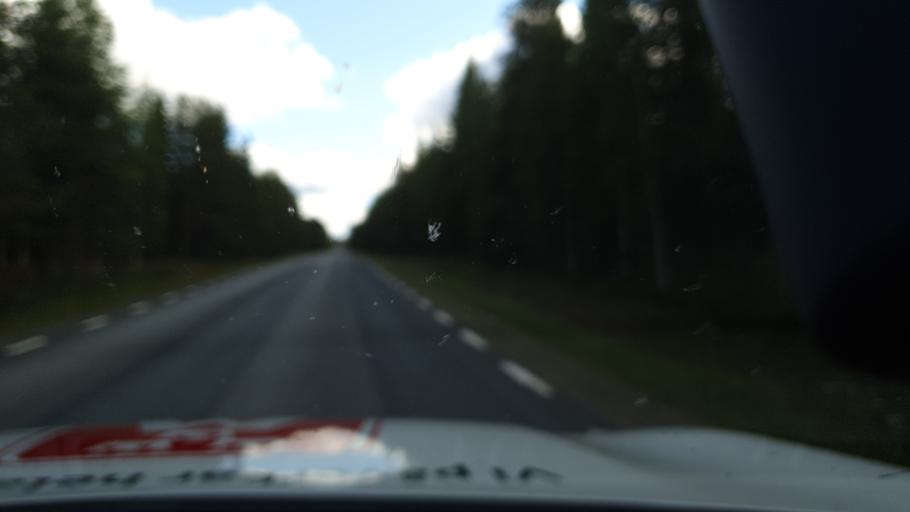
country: SE
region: Vaesterbotten
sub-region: Mala Kommun
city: Mala
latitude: 65.1487
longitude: 18.6212
